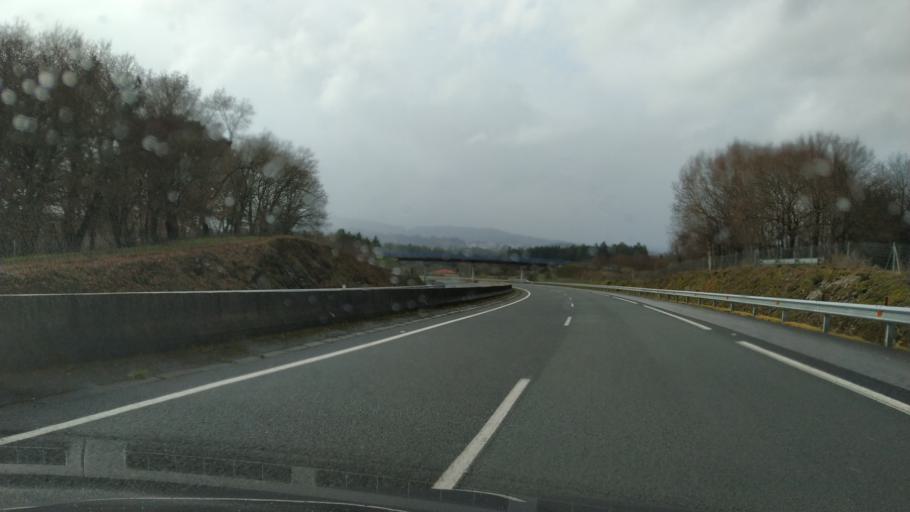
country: ES
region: Galicia
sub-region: Provincia de Pontevedra
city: Silleda
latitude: 42.7180
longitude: -8.2604
